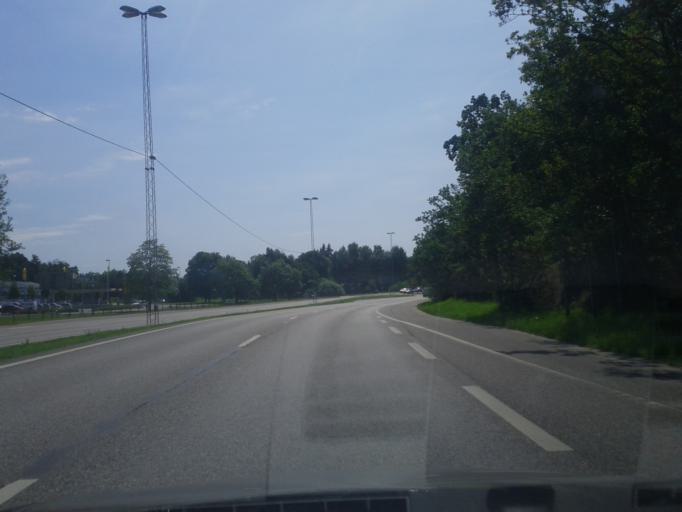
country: SE
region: Stockholm
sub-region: Huddinge Kommun
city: Huddinge
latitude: 59.2583
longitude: 18.0129
